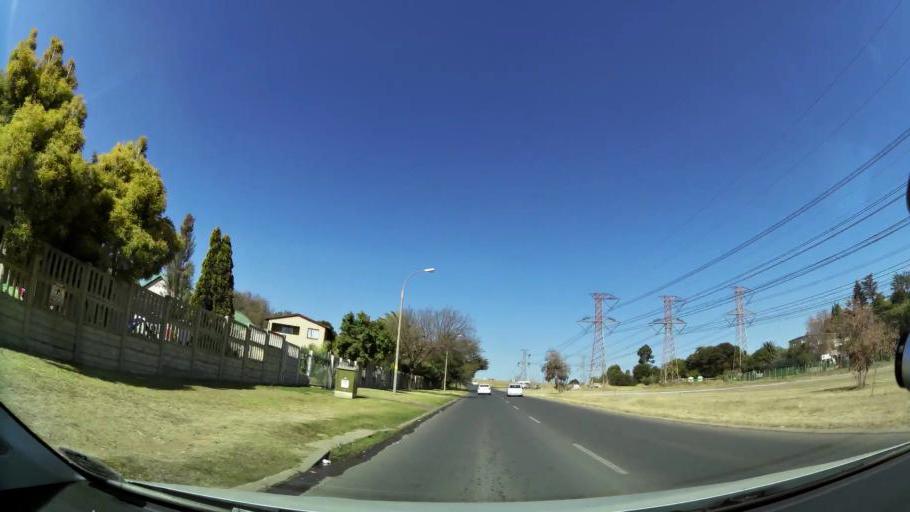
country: ZA
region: Gauteng
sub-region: City of Johannesburg Metropolitan Municipality
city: Modderfontein
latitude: -26.0598
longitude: 28.2152
